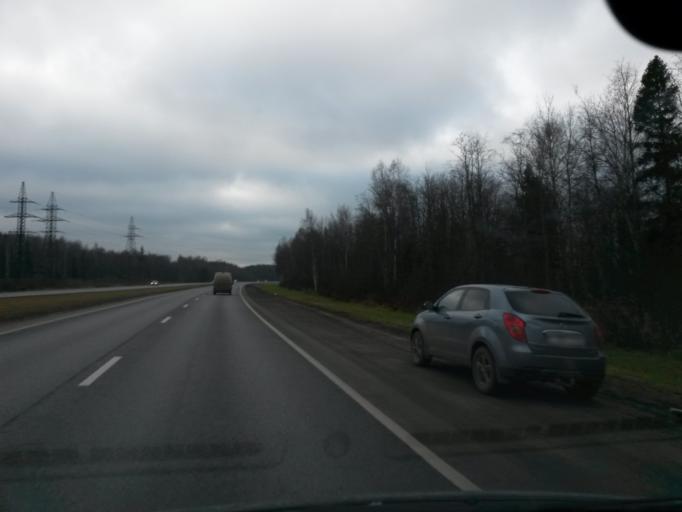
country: RU
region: Jaroslavl
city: Krasnyye Tkachi
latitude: 57.4961
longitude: 39.7840
